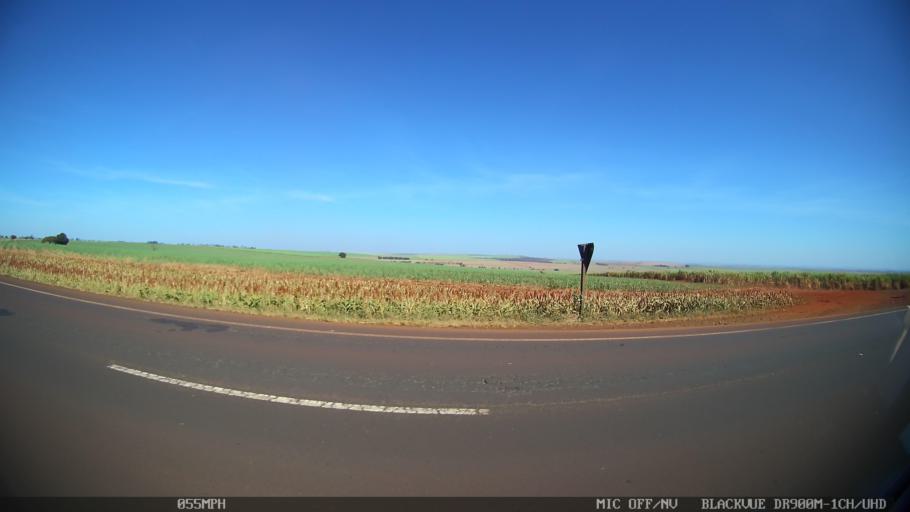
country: BR
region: Sao Paulo
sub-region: Ipua
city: Ipua
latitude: -20.4767
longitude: -48.0902
